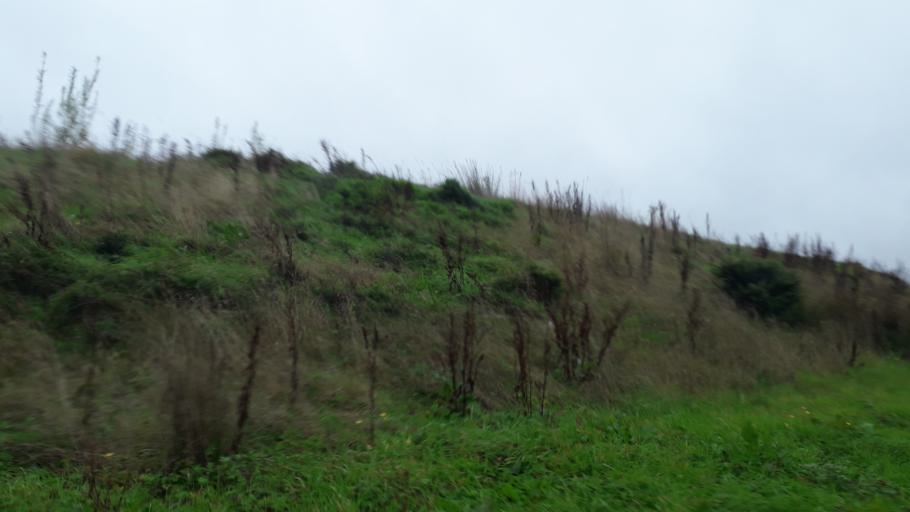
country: IE
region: Connaught
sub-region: Roscommon
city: Ballaghaderreen
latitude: 53.8893
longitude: -8.4947
